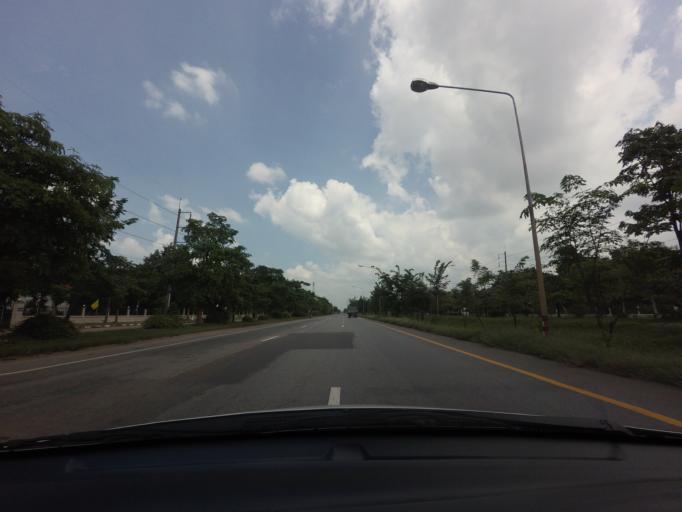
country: TH
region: Prachin Buri
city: Kabin Buri
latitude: 13.9482
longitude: 101.7133
